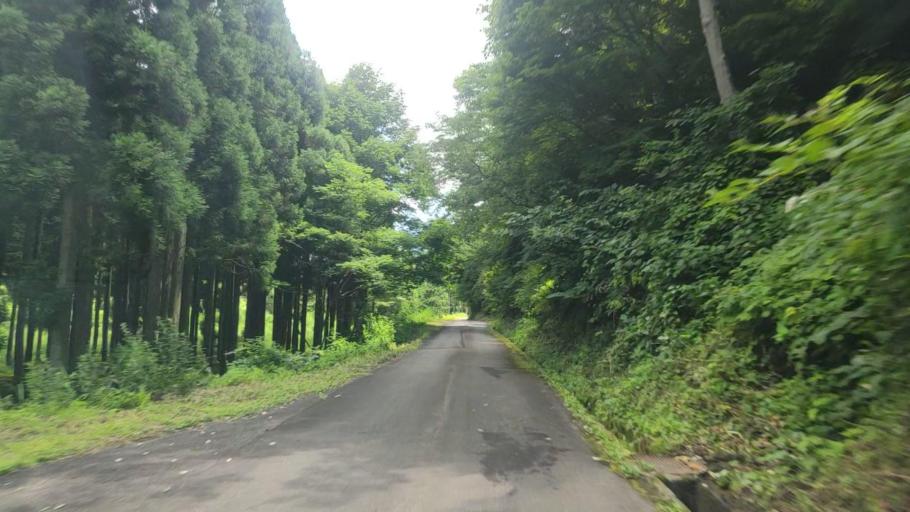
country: JP
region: Fukui
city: Ono
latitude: 35.8125
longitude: 136.4613
